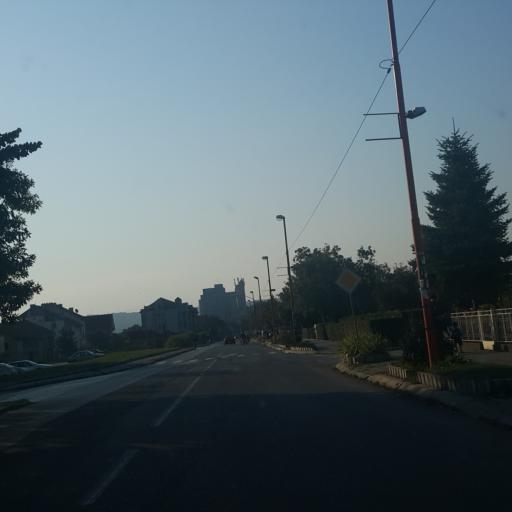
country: RS
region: Central Serbia
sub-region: Zajecarski Okrug
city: Zajecar
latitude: 43.9089
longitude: 22.2616
